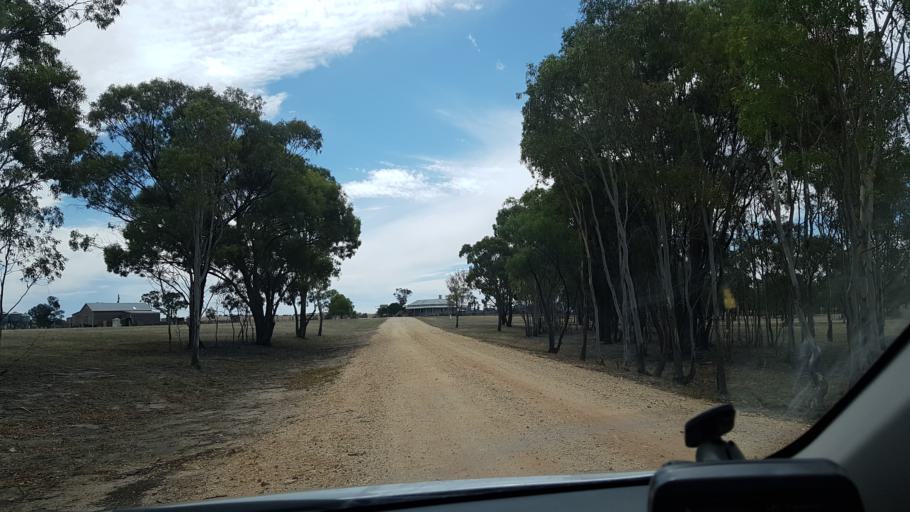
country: AU
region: Victoria
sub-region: Horsham
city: Horsham
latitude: -36.6839
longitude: 141.7745
